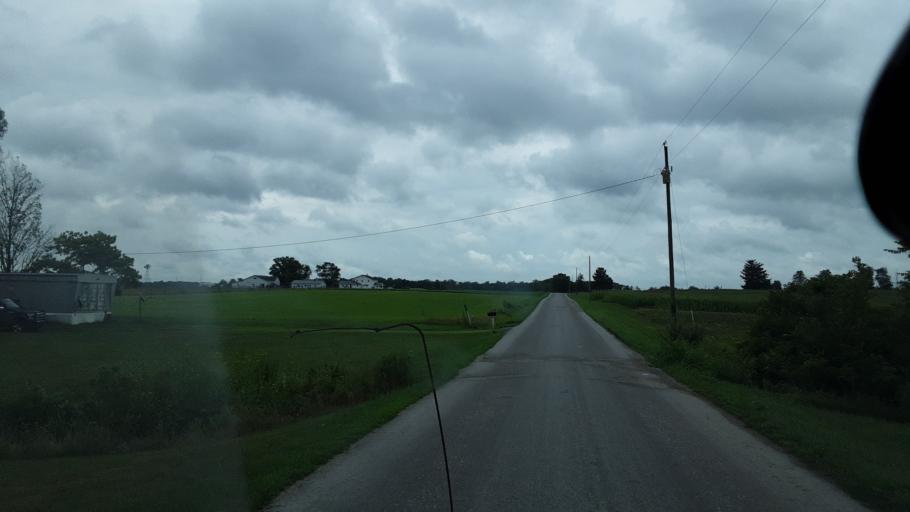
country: US
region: Indiana
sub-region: Adams County
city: Geneva
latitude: 40.5376
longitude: -84.9913
